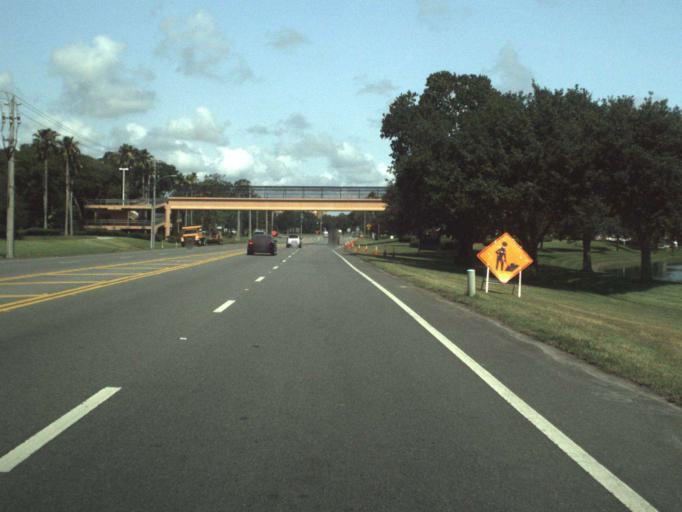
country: US
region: Florida
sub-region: Volusia County
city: Daytona Beach
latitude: 29.1906
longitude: -81.0476
